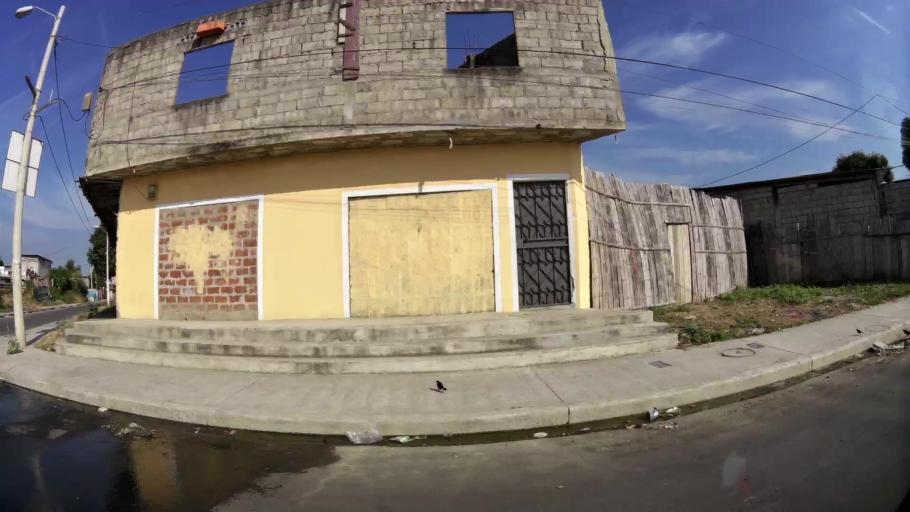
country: EC
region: Guayas
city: Eloy Alfaro
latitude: -2.0829
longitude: -79.9240
